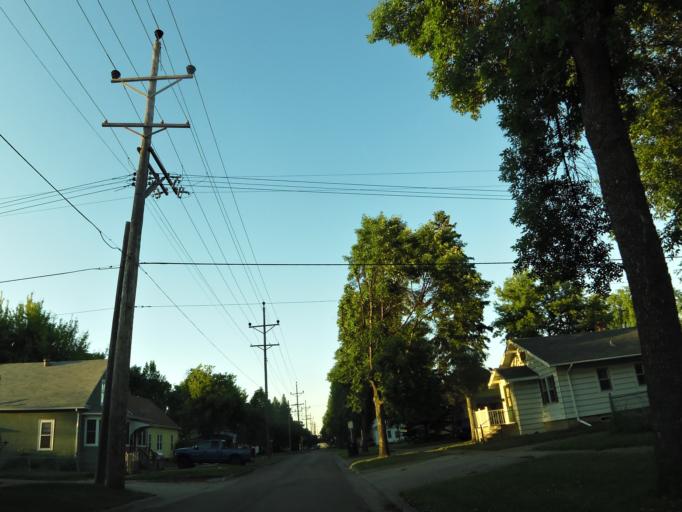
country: US
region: North Dakota
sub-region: Grand Forks County
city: Grand Forks
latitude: 47.9271
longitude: -97.0428
